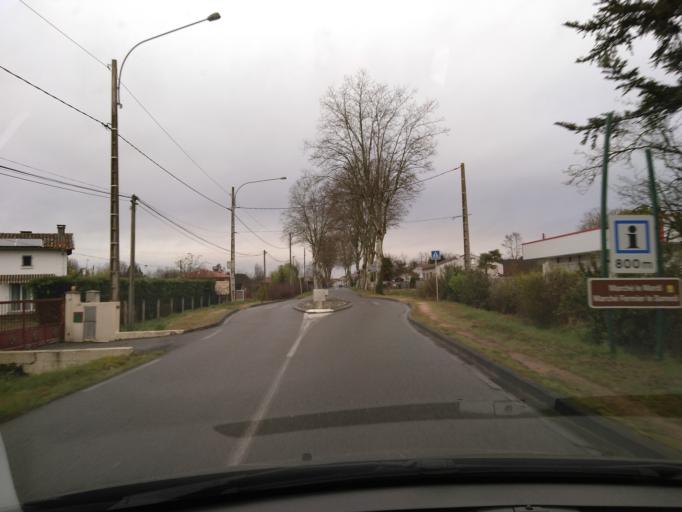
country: FR
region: Midi-Pyrenees
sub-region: Departement de la Haute-Garonne
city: Montesquieu-Volvestre
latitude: 43.1988
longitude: 1.2309
